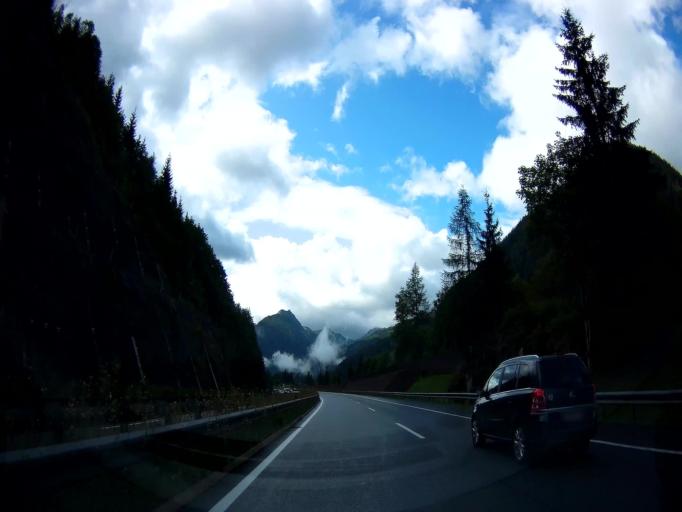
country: AT
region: Salzburg
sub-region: Politischer Bezirk Sankt Johann im Pongau
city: Flachau
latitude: 47.3228
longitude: 13.3944
